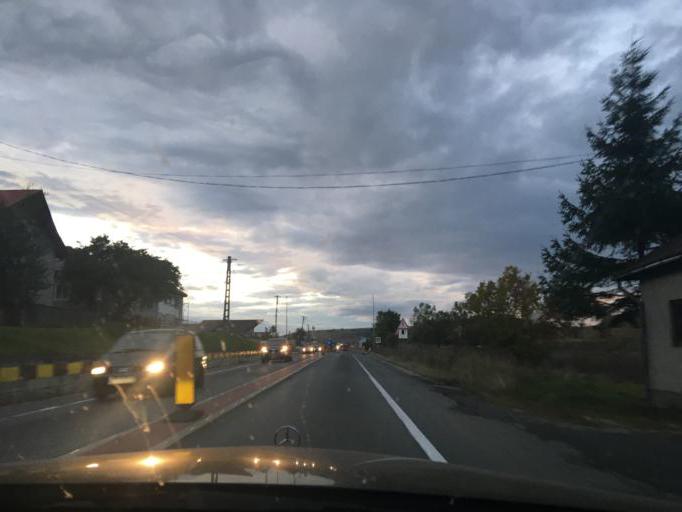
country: RO
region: Cluj
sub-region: Comuna Izvoru Crisului
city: Izvoru Crisului
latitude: 46.8154
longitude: 23.1793
